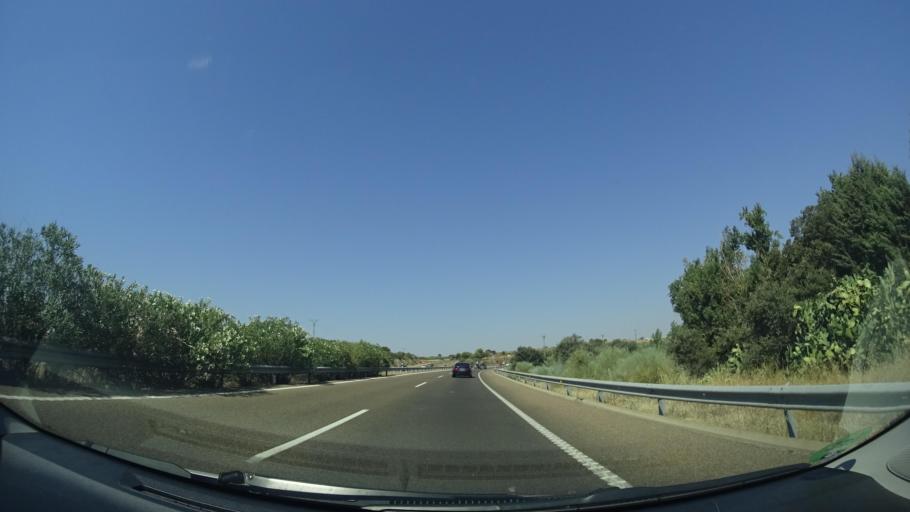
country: ES
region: Extremadura
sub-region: Provincia de Badajoz
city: San Pedro de Merida
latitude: 38.9458
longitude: -6.1811
